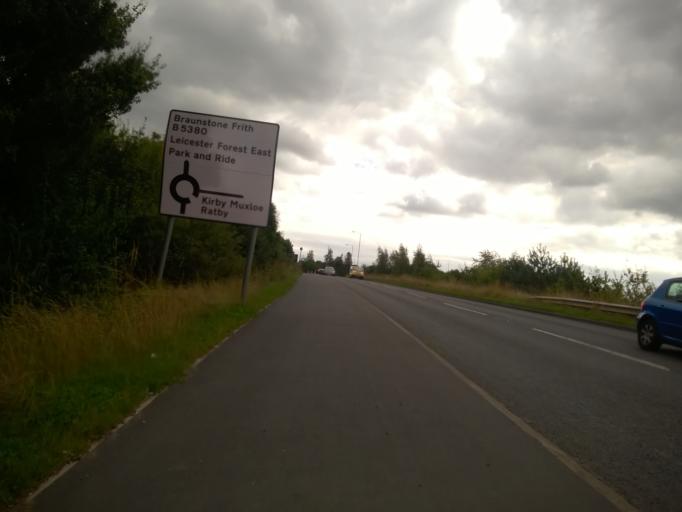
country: GB
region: England
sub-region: Leicestershire
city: Kirby Muxloe
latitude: 52.6375
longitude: -1.2178
